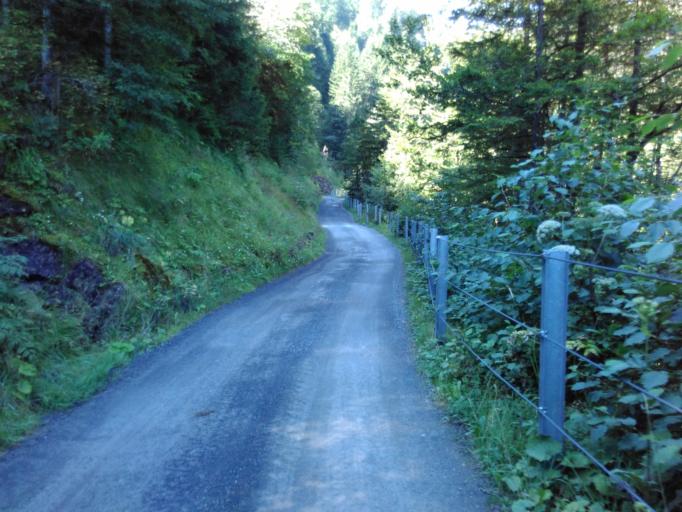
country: CH
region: Schwyz
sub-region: Bezirk Schwyz
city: Arth
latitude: 47.0378
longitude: 8.5025
